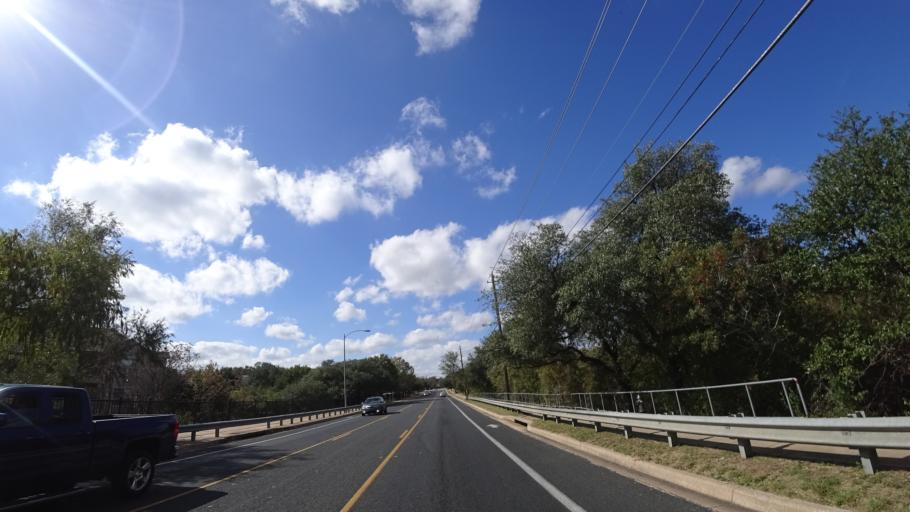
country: US
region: Texas
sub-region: Travis County
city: Wells Branch
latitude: 30.4118
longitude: -97.7256
